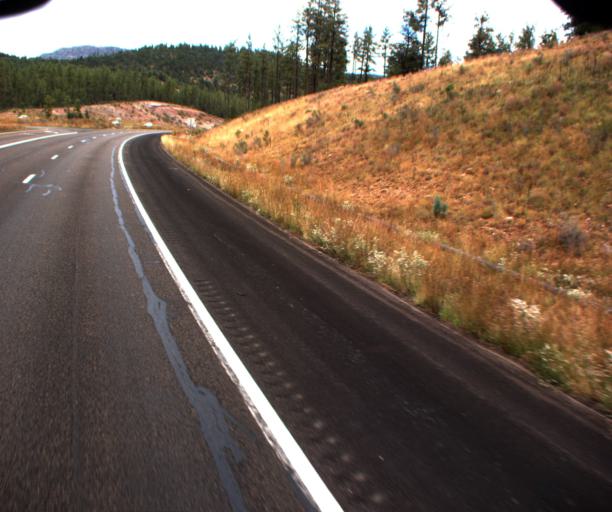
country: US
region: Arizona
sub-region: Gila County
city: Star Valley
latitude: 34.3163
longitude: -111.1138
